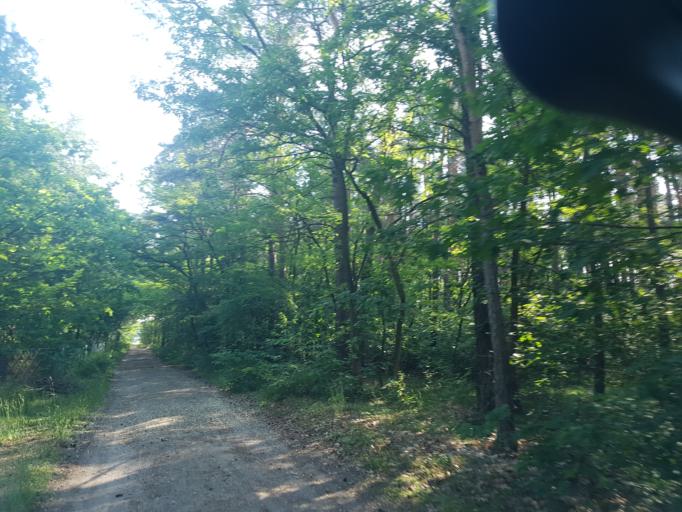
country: DE
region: Brandenburg
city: Finsterwalde
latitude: 51.5685
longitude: 13.6794
